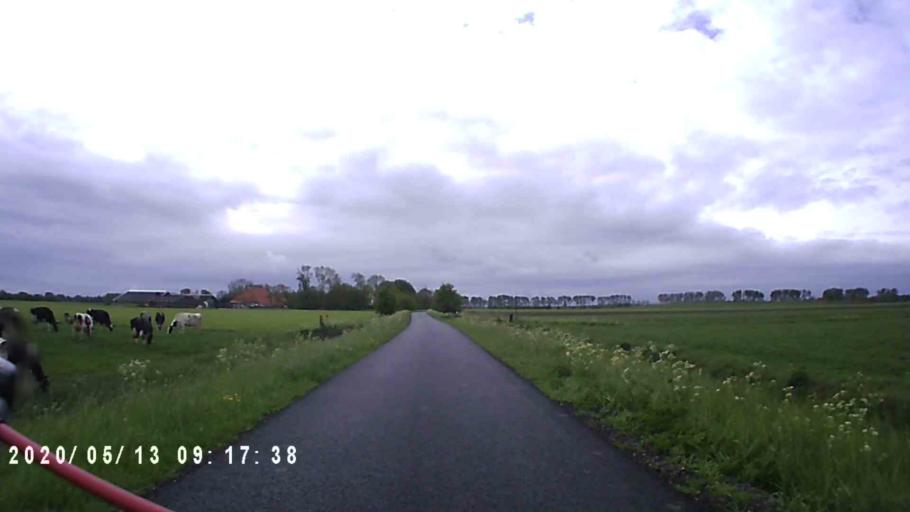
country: NL
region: Groningen
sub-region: Gemeente Zuidhorn
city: Noordhorn
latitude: 53.2678
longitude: 6.4147
